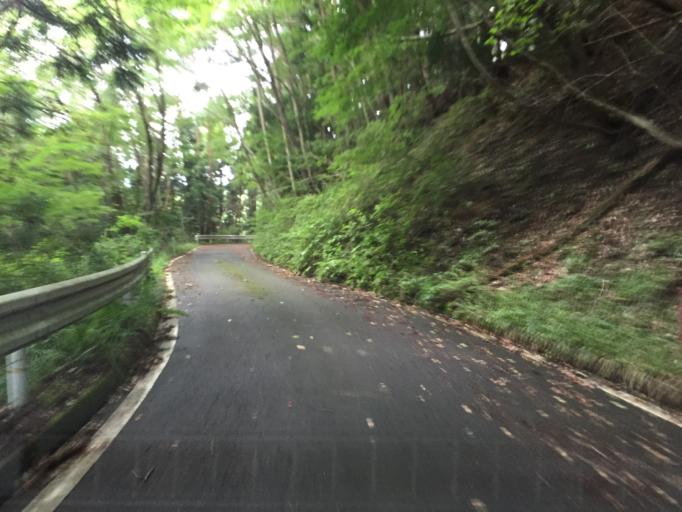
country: JP
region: Fukushima
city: Motomiya
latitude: 37.5499
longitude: 140.3017
